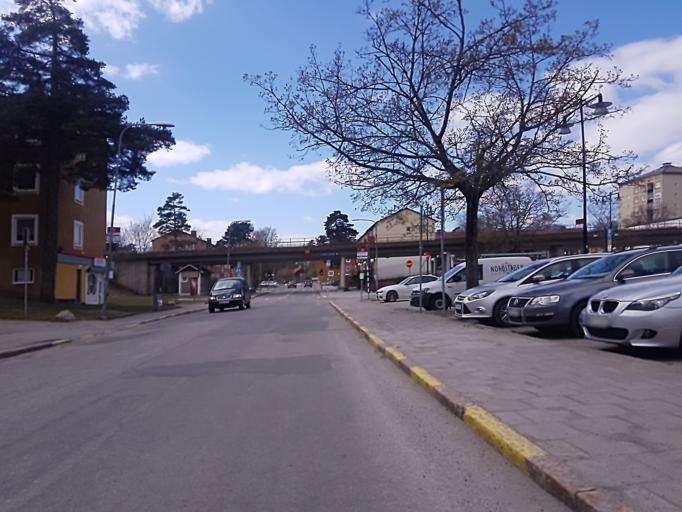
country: SE
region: Stockholm
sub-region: Nacka Kommun
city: Nacka
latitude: 59.2837
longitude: 18.1165
